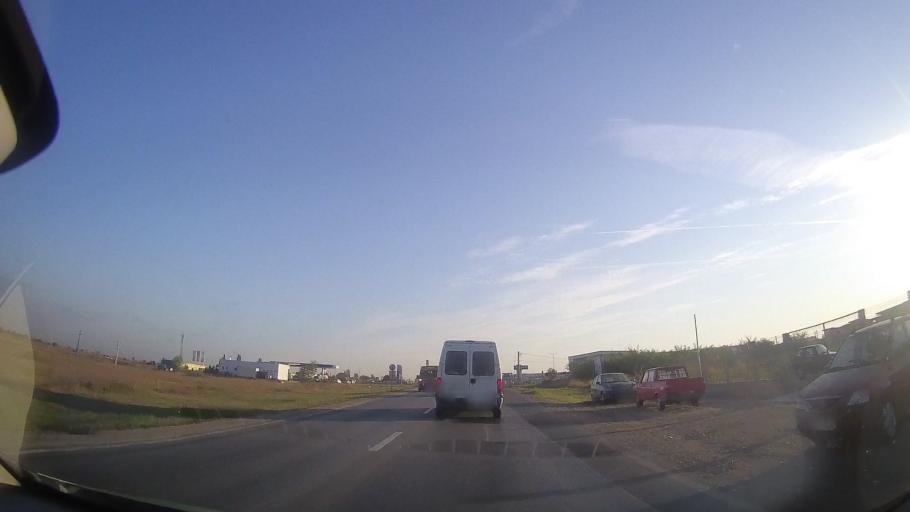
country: RO
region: Timis
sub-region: Comuna Dumbravita
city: Dumbravita
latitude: 45.8119
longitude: 21.2609
